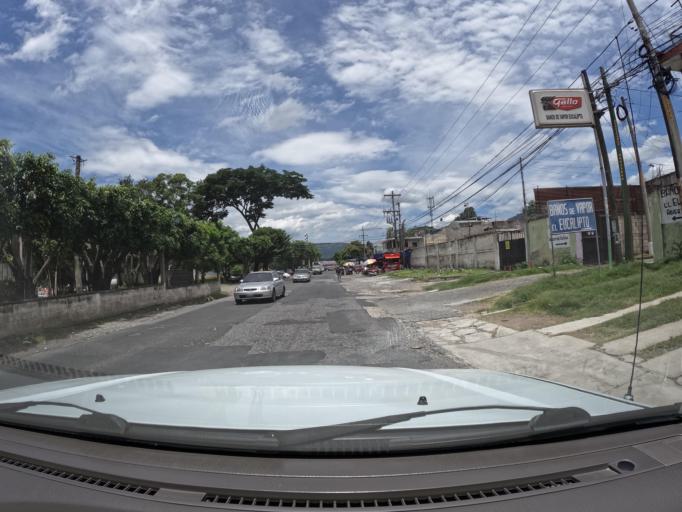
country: GT
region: Guatemala
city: Amatitlan
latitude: 14.4876
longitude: -90.6174
